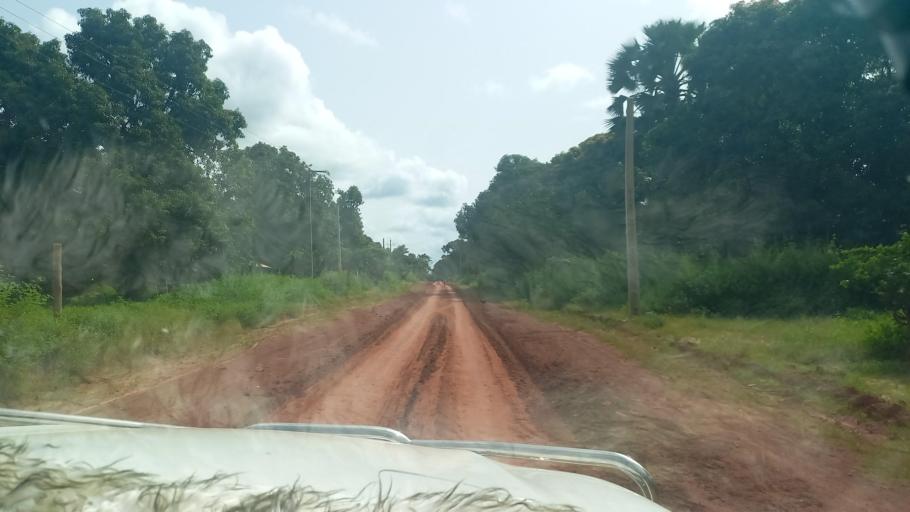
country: SN
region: Ziguinchor
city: Bignona
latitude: 12.7562
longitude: -16.2695
